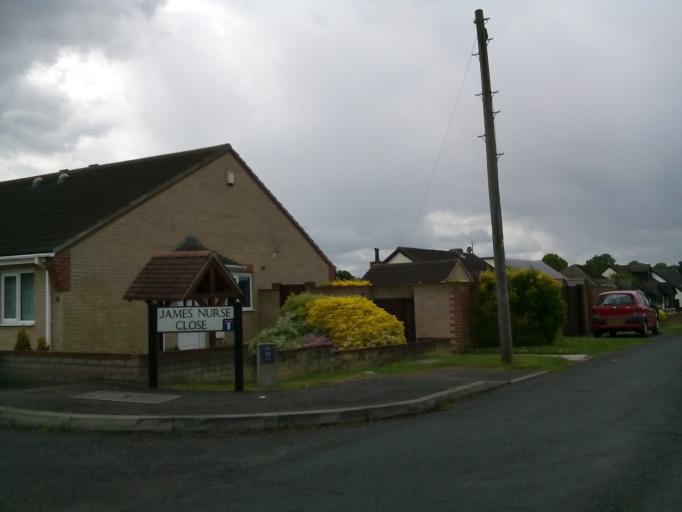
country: GB
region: England
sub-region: Cambridgeshire
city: Fulbourn
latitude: 52.1886
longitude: 0.1856
